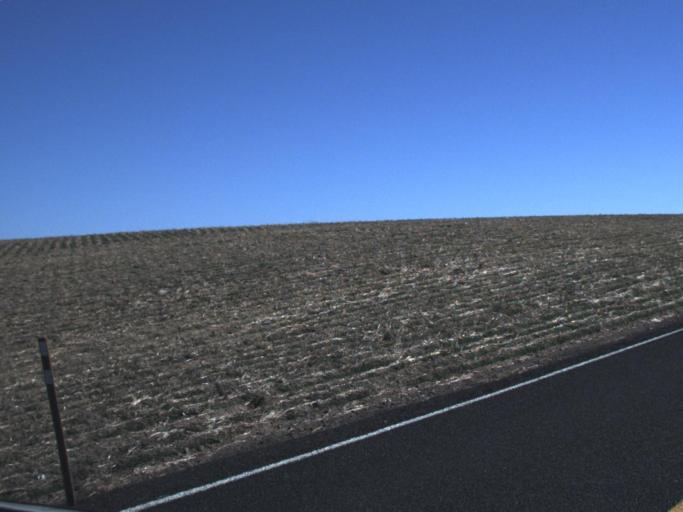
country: US
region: Washington
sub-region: Adams County
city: Ritzville
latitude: 46.8837
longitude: -118.5661
